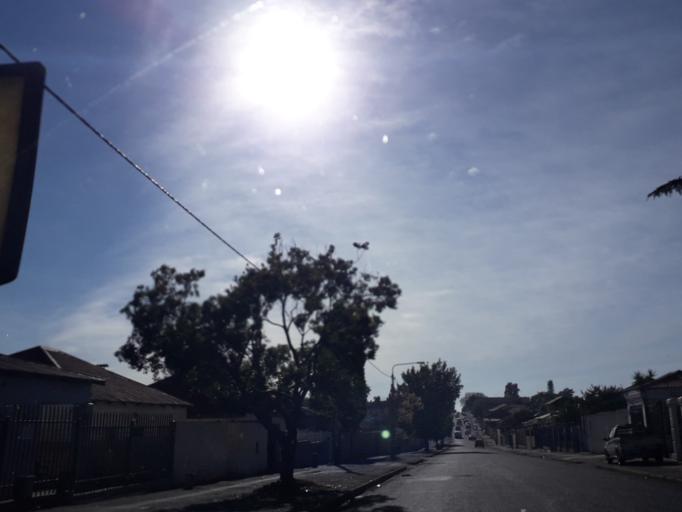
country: ZA
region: Gauteng
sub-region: City of Johannesburg Metropolitan Municipality
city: Johannesburg
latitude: -26.1908
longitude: 27.9940
